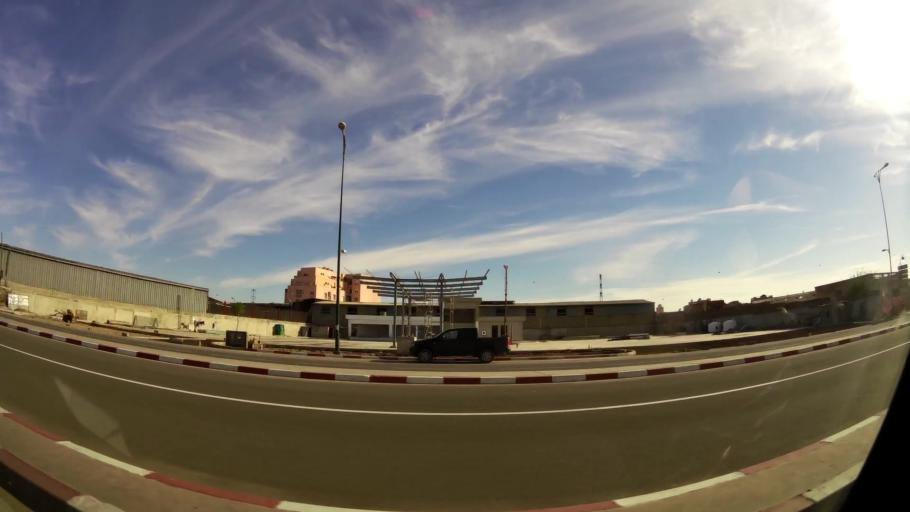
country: MA
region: Marrakech-Tensift-Al Haouz
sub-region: Marrakech
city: Marrakesh
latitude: 31.6269
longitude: -8.0337
